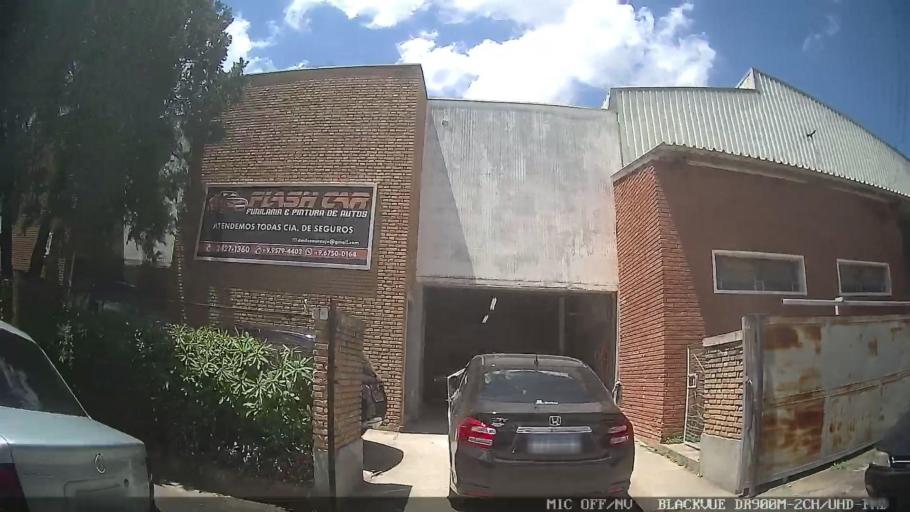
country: BR
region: Sao Paulo
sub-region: Atibaia
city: Atibaia
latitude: -23.1084
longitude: -46.5589
